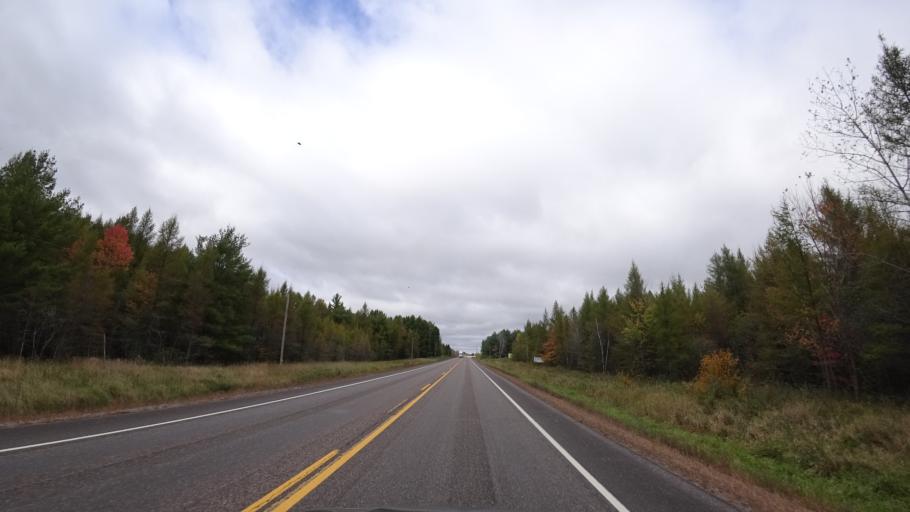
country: US
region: Wisconsin
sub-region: Rusk County
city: Ladysmith
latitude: 45.4121
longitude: -91.1105
